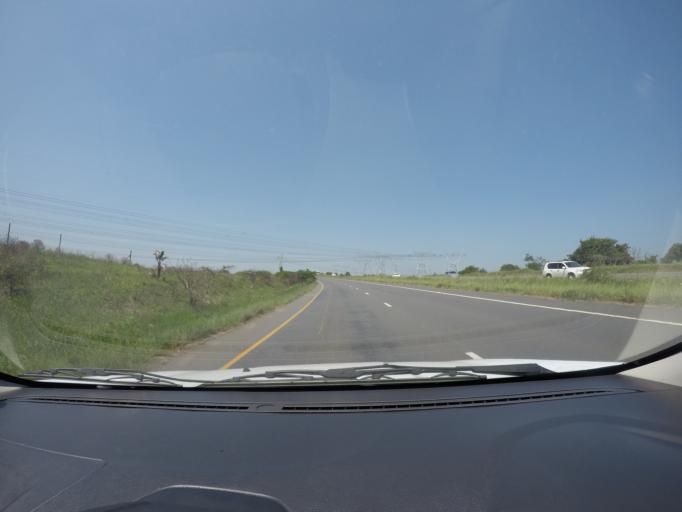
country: ZA
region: KwaZulu-Natal
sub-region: uThungulu District Municipality
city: Richards Bay
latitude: -28.7794
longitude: 32.0016
